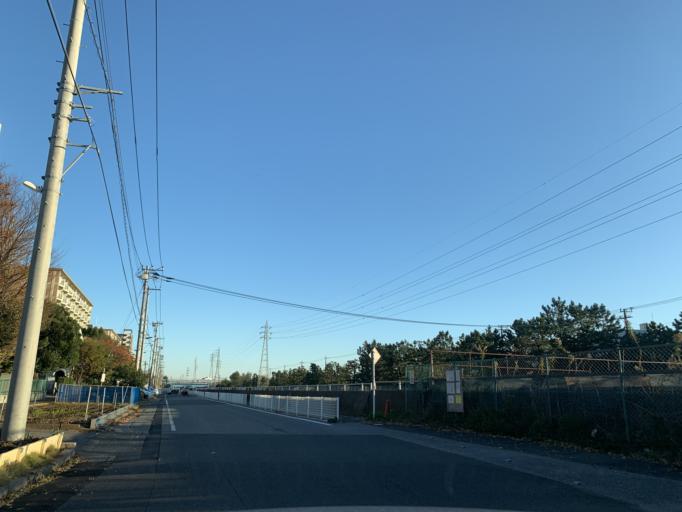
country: JP
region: Tokyo
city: Urayasu
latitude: 35.6626
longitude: 139.9077
